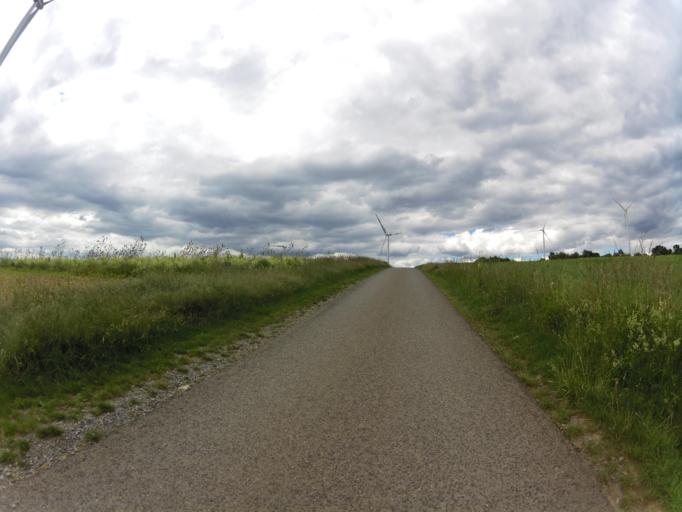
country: DE
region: Bavaria
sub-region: Regierungsbezirk Unterfranken
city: Retzstadt
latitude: 49.8877
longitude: 9.8867
